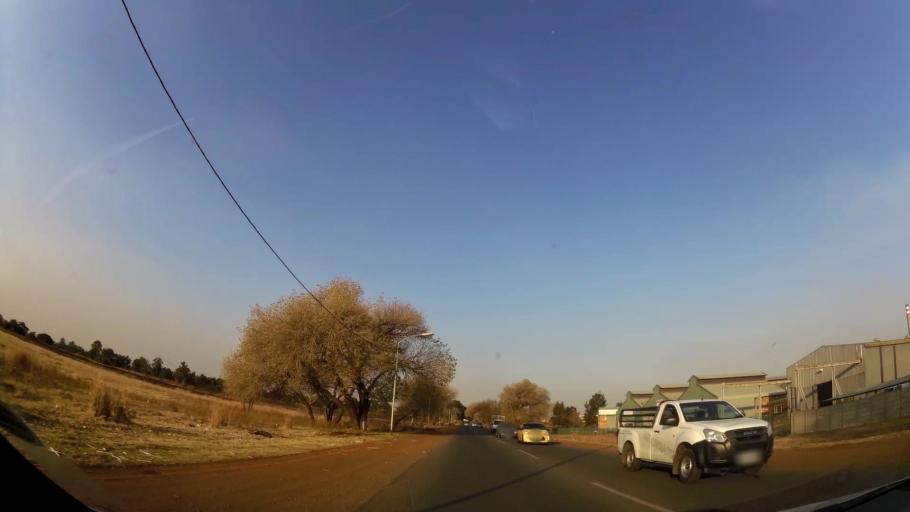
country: ZA
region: Gauteng
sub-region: Ekurhuleni Metropolitan Municipality
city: Springs
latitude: -26.2537
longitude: 28.4092
